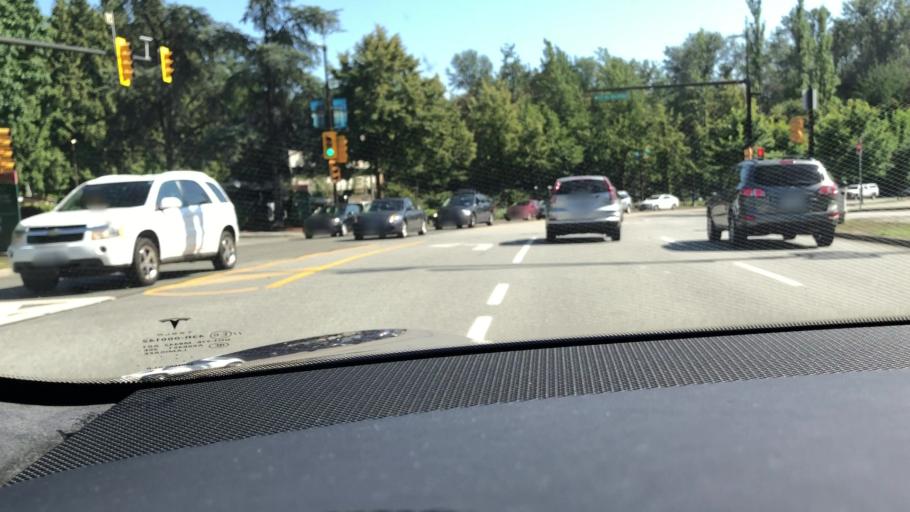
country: CA
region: British Columbia
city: Burnaby
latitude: 49.2435
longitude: -122.9747
